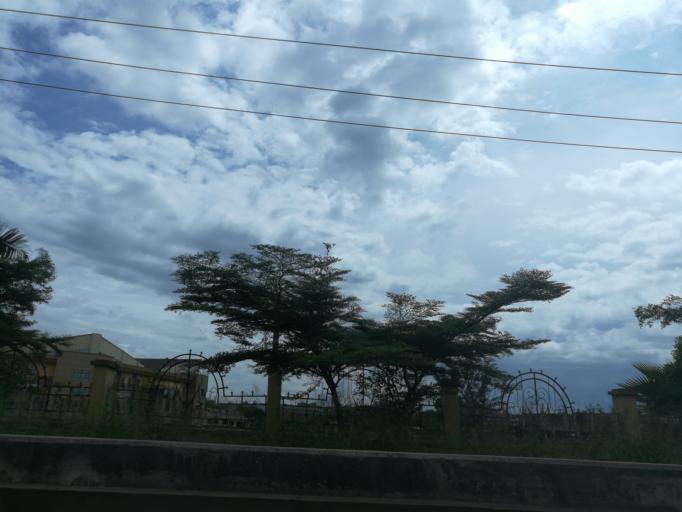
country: NG
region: Lagos
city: Somolu
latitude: 6.5547
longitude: 3.3725
